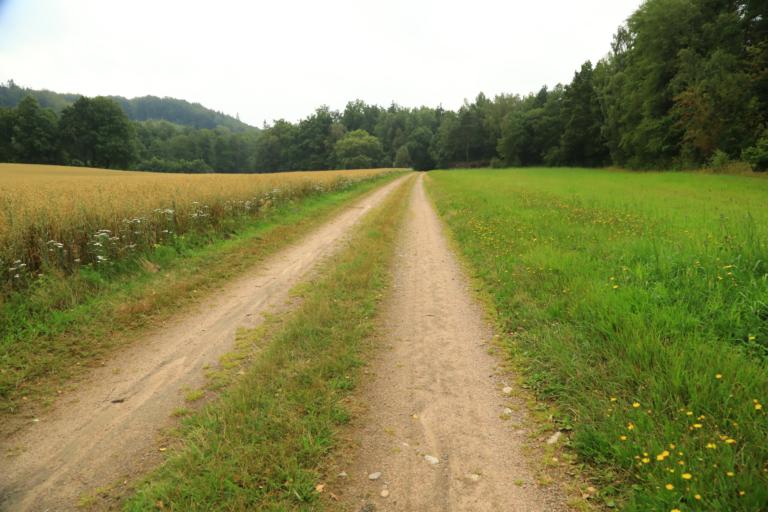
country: SE
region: Halland
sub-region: Falkenbergs Kommun
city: Falkenberg
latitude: 57.1143
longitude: 12.6850
